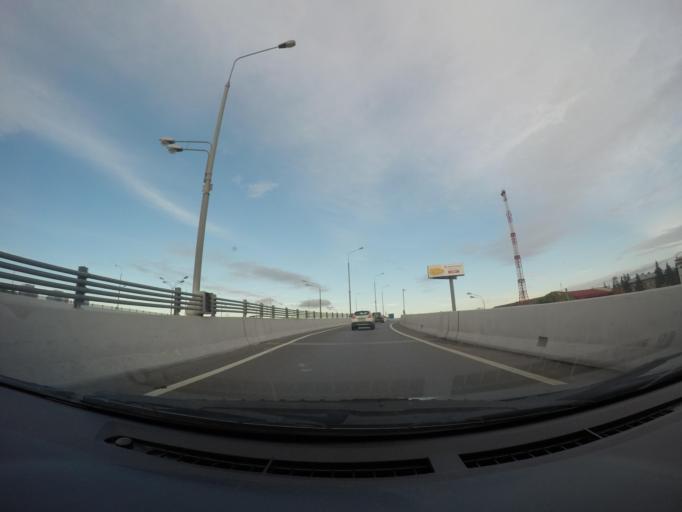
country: RU
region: Moskovskaya
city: Razvilka
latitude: 55.5936
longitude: 37.7344
